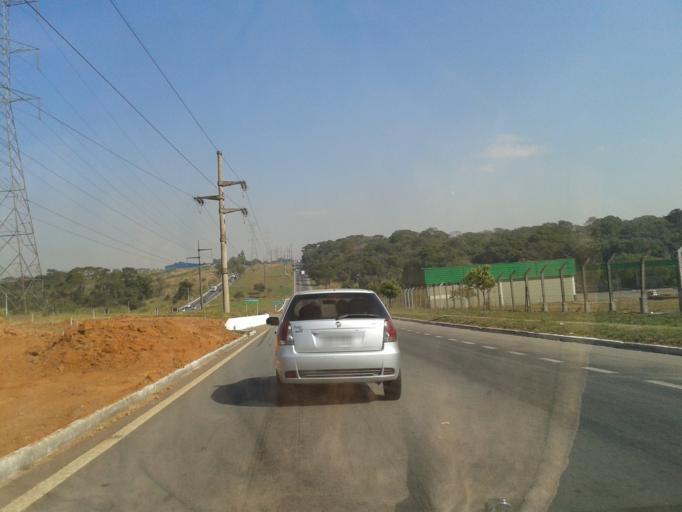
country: BR
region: Goias
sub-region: Aparecida De Goiania
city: Aparecida de Goiania
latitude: -16.7858
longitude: -49.2562
